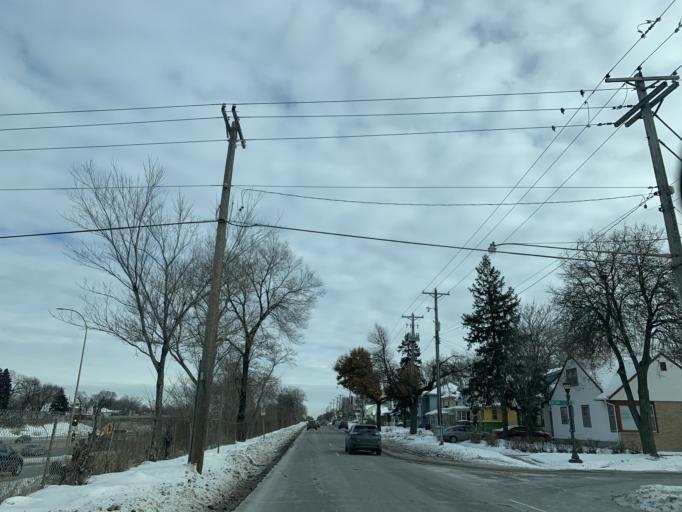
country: US
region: Minnesota
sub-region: Ramsey County
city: Falcon Heights
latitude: 44.9513
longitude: -93.1444
